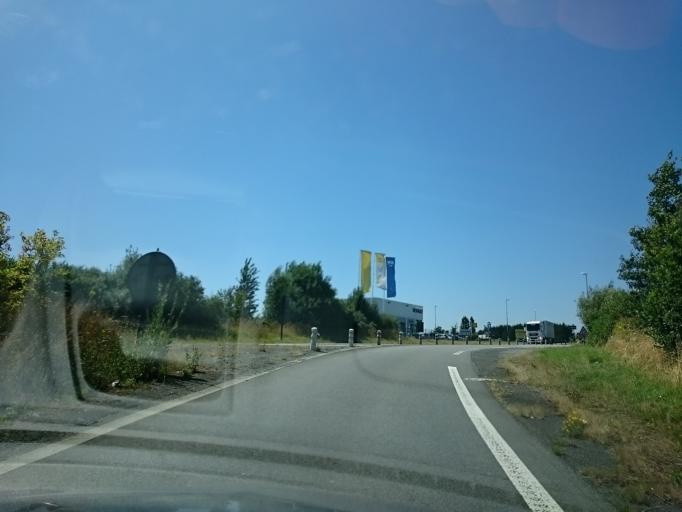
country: FR
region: Brittany
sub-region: Departement d'Ille-et-Vilaine
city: Corps-Nuds
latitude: 47.9894
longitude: -1.5892
